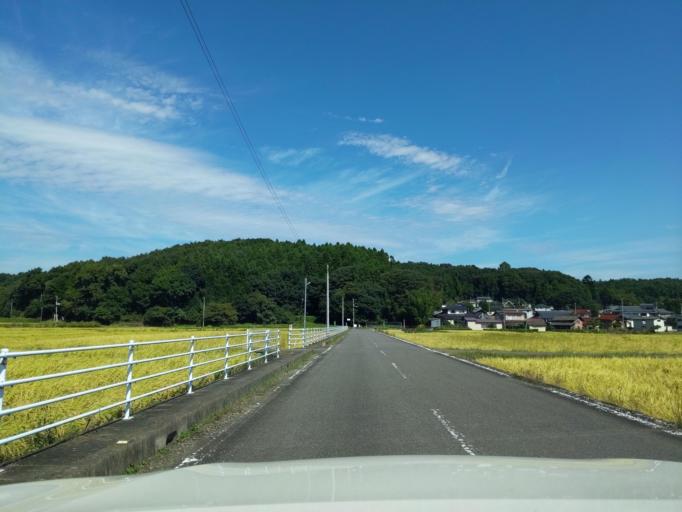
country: JP
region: Fukushima
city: Koriyama
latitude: 37.3717
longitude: 140.2866
